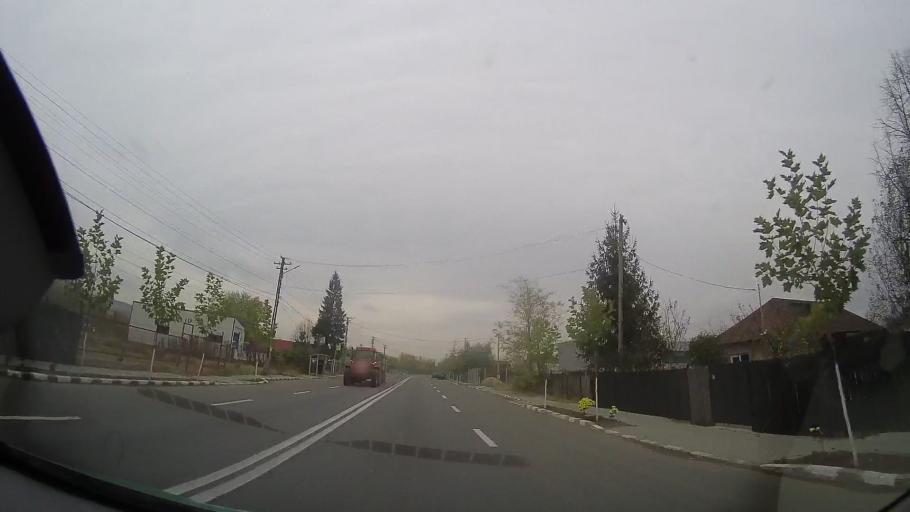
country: RO
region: Prahova
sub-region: Oras Urlati
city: Urlati
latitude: 44.9732
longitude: 26.2333
